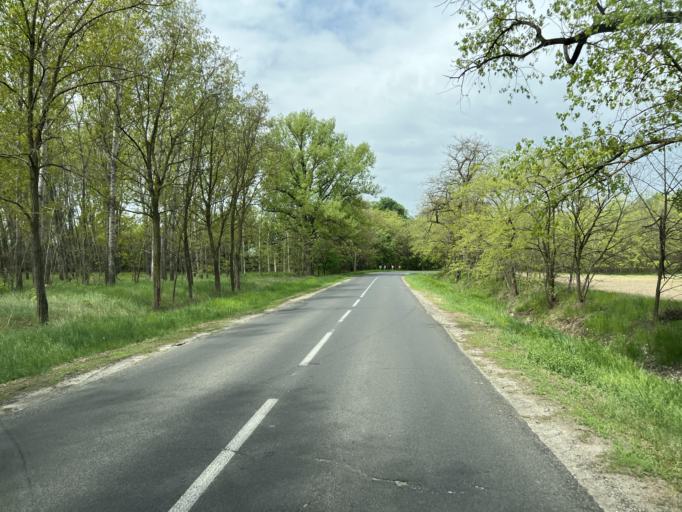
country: HU
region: Pest
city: Tortel
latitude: 47.1454
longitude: 19.8709
